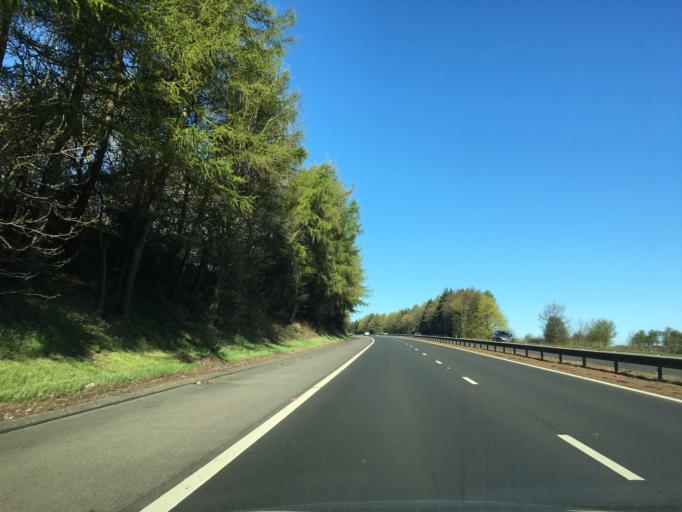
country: GB
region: Scotland
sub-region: Stirling
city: Plean
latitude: 56.0666
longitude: -3.8729
